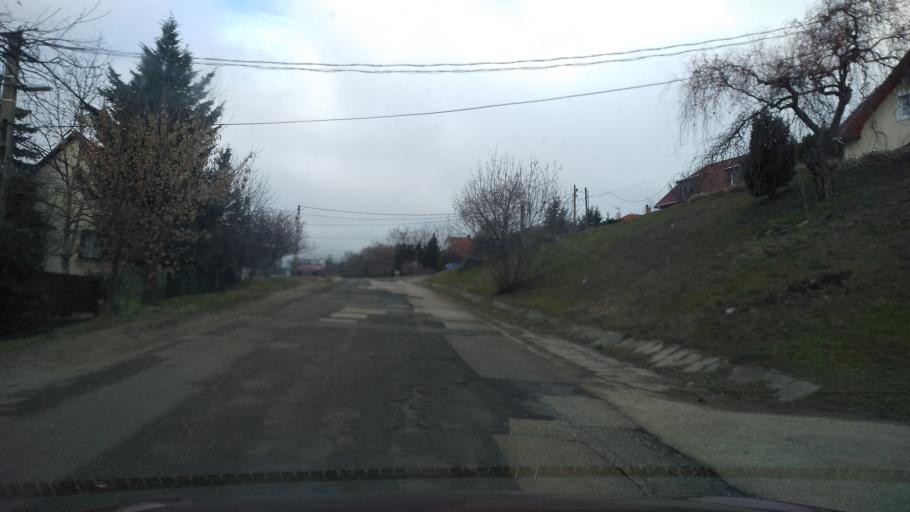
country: HU
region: Pest
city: Szentendre
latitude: 47.6841
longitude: 19.0490
